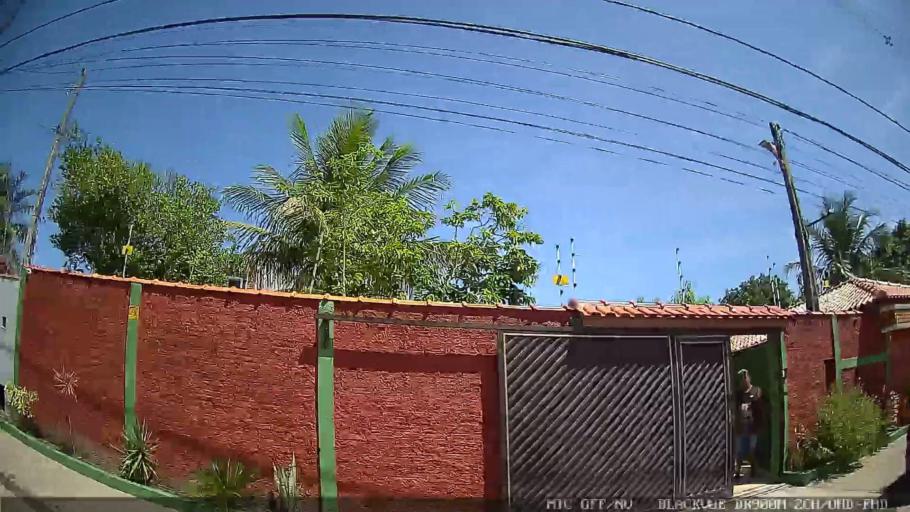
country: BR
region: Sao Paulo
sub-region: Peruibe
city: Peruibe
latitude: -24.2994
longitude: -46.9946
